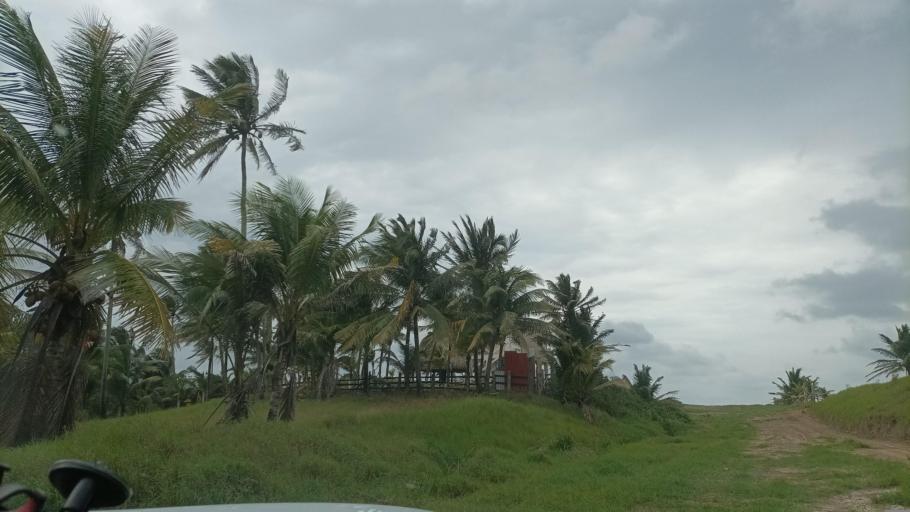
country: MX
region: Veracruz
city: Agua Dulce
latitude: 18.2079
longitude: -94.1480
